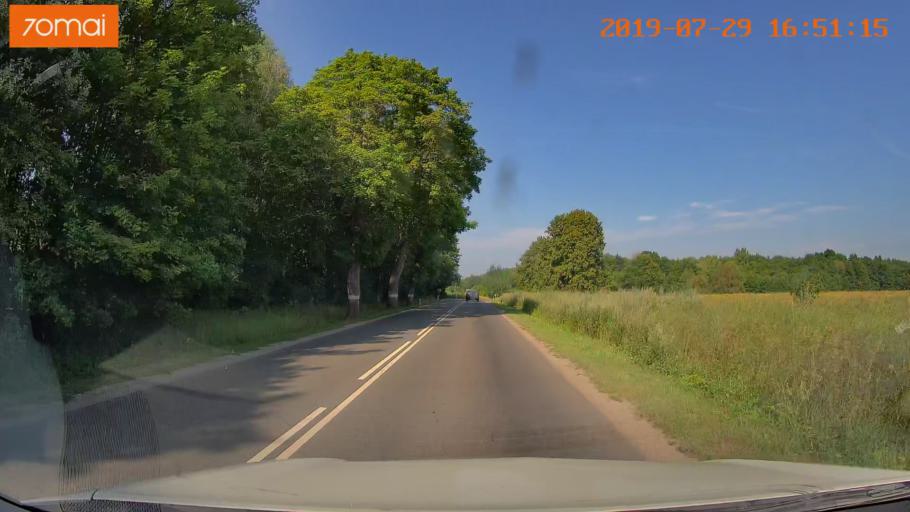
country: RU
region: Kaliningrad
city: Primorsk
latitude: 54.8081
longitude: 20.0651
